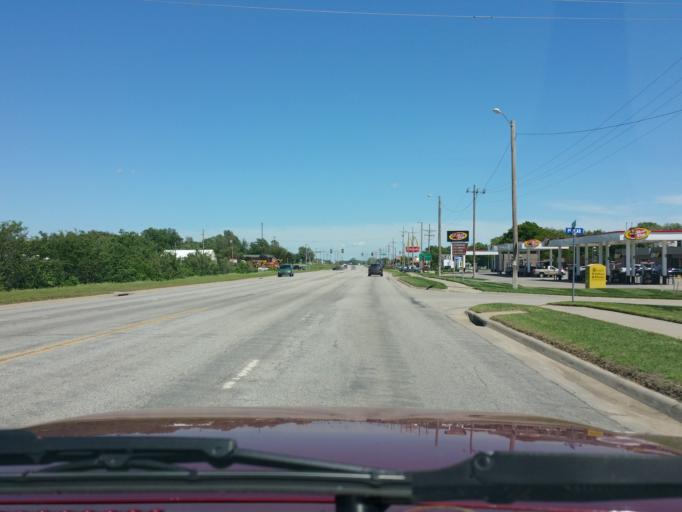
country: US
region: Kansas
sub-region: Pottawatomie County
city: Wamego
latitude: 39.2101
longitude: -96.3085
